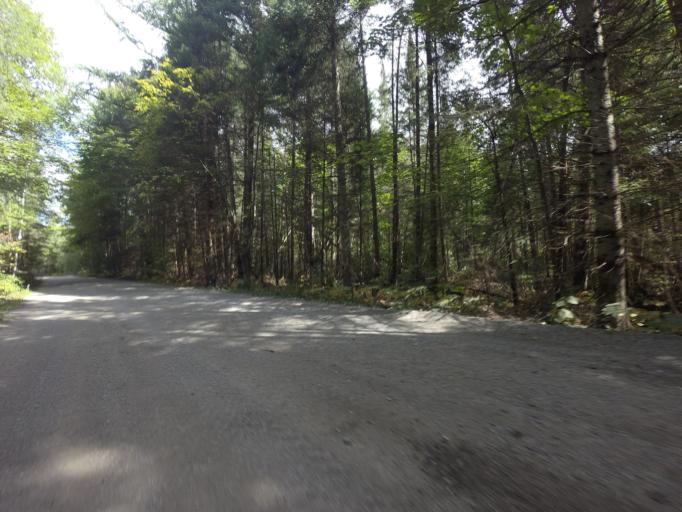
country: CA
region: Ontario
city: Omemee
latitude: 44.7451
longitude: -78.6647
